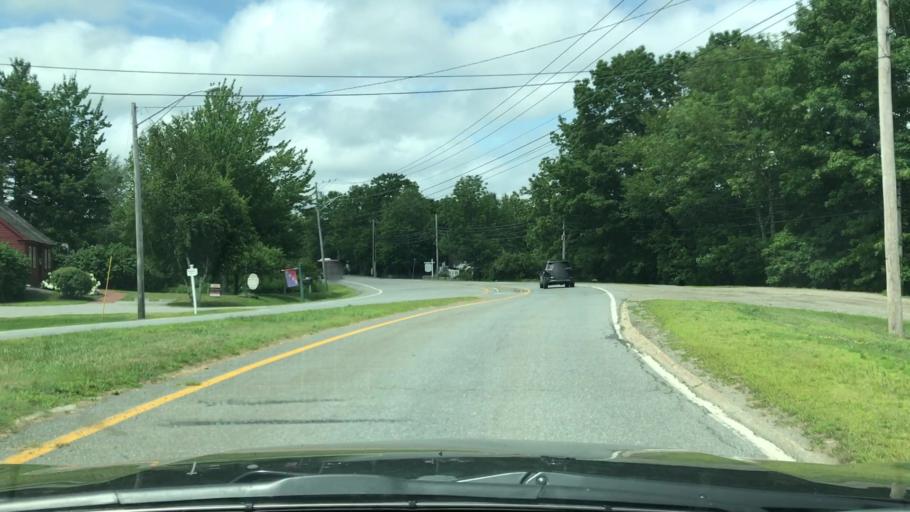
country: US
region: Maine
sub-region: Waldo County
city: Belfast
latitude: 44.4085
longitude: -68.9930
